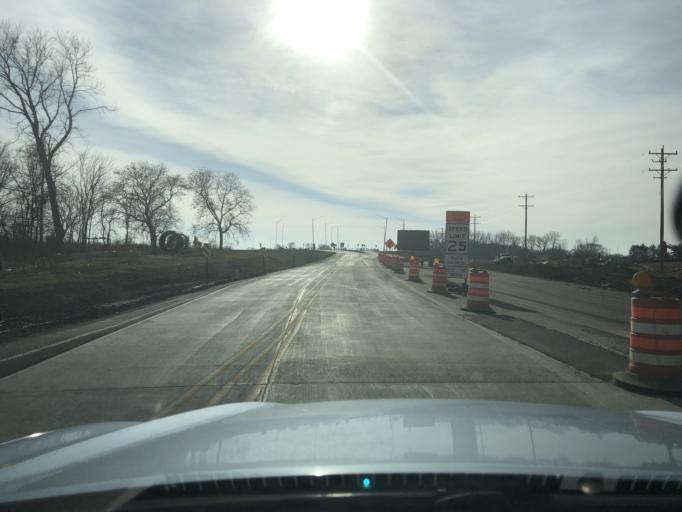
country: US
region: Illinois
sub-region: McHenry County
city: Marengo
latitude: 42.1819
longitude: -88.6180
